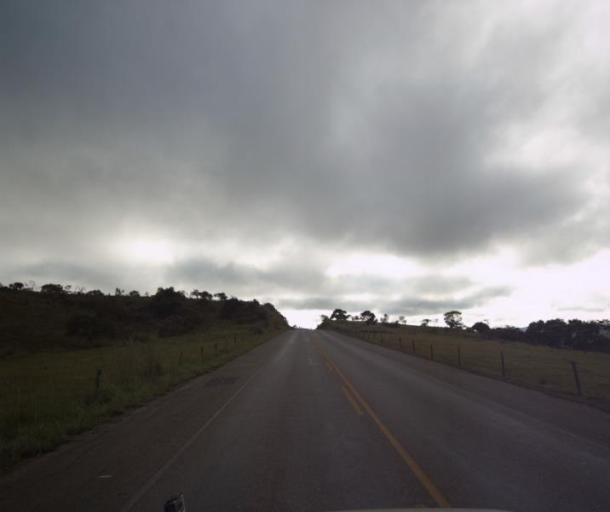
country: BR
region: Goias
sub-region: Pirenopolis
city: Pirenopolis
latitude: -15.7367
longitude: -48.7193
